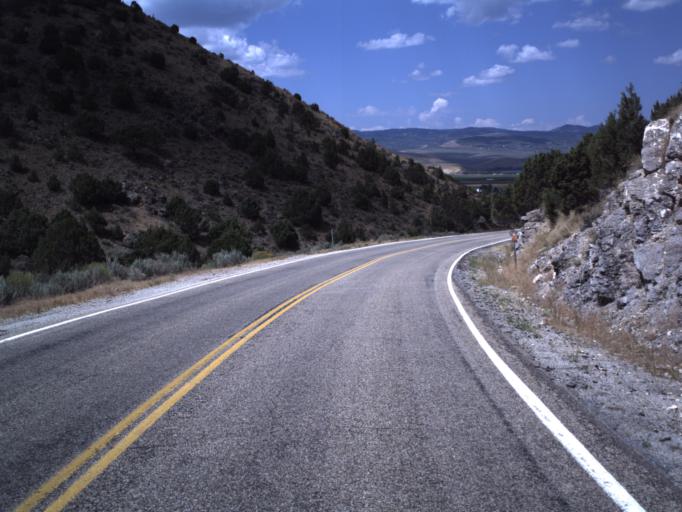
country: US
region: Utah
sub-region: Rich County
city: Randolph
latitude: 41.8248
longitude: -111.3091
